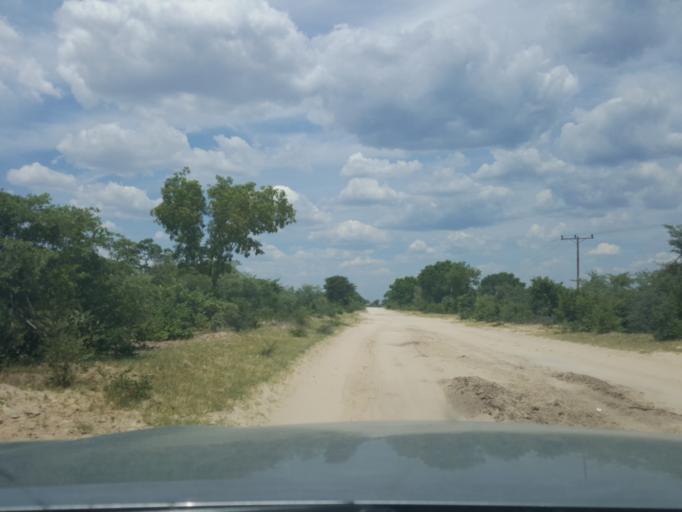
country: BW
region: North West
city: Shakawe
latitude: -18.4783
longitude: 22.1122
